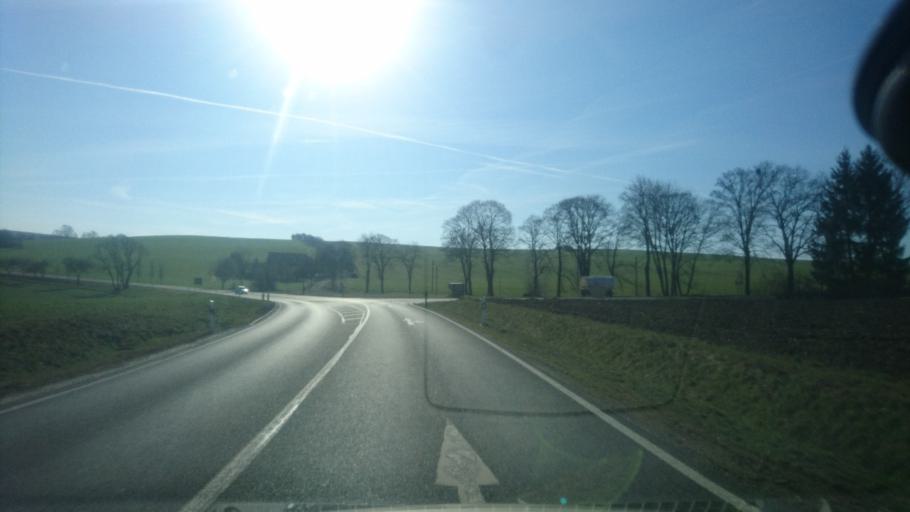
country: DE
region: Saxony
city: Neuensalz
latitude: 50.4883
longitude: 12.2211
